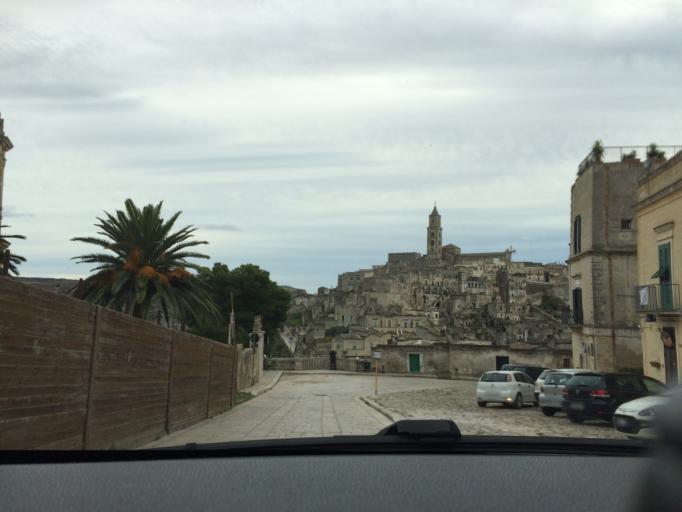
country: IT
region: Basilicate
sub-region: Provincia di Matera
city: Matera
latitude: 40.6702
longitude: 16.6094
